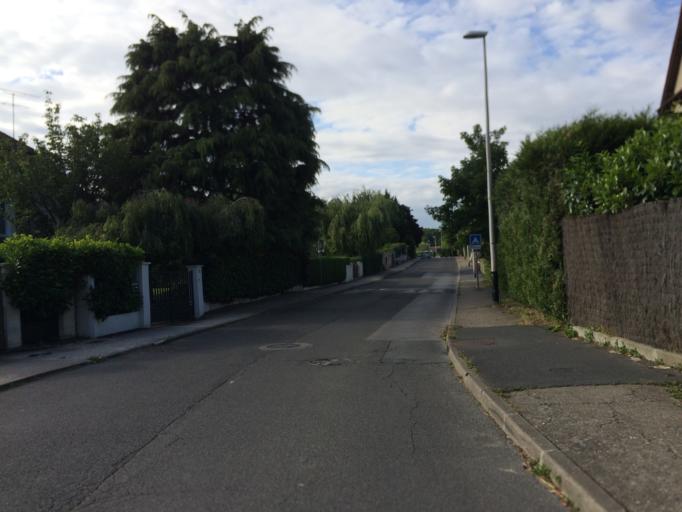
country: FR
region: Ile-de-France
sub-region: Departement de l'Essonne
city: Verrieres-le-Buisson
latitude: 48.7550
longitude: 2.2695
